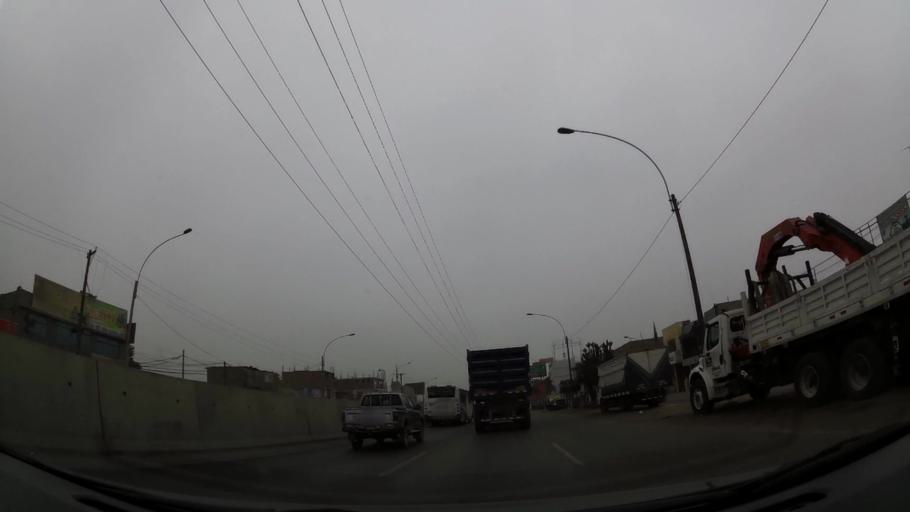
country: PE
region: Lima
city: Ventanilla
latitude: -11.8578
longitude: -77.0833
